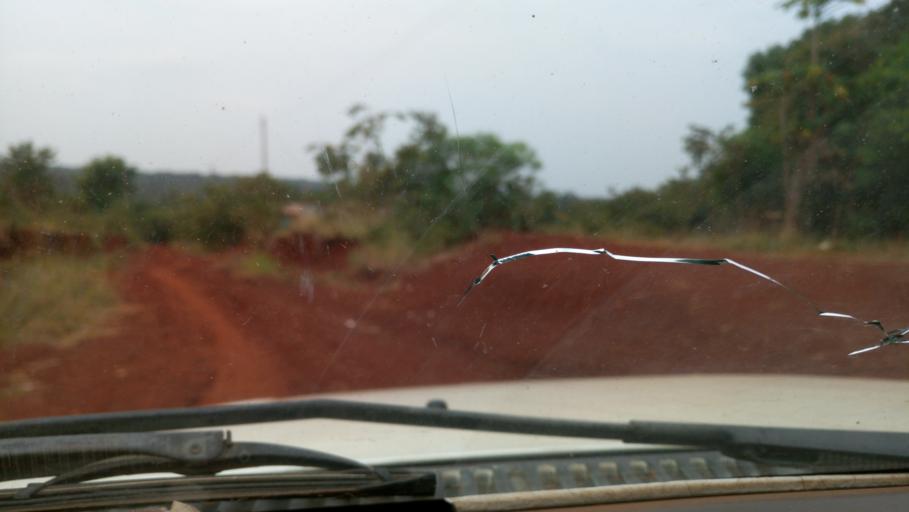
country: KE
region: Murang'a District
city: Maragua
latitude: -0.7704
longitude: 37.1874
